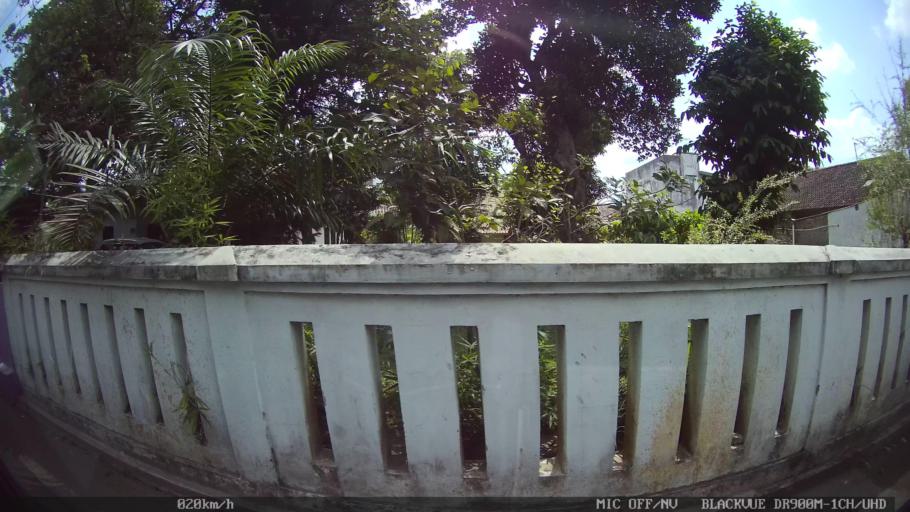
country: ID
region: Daerah Istimewa Yogyakarta
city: Gamping Lor
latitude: -7.8063
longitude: 110.3481
